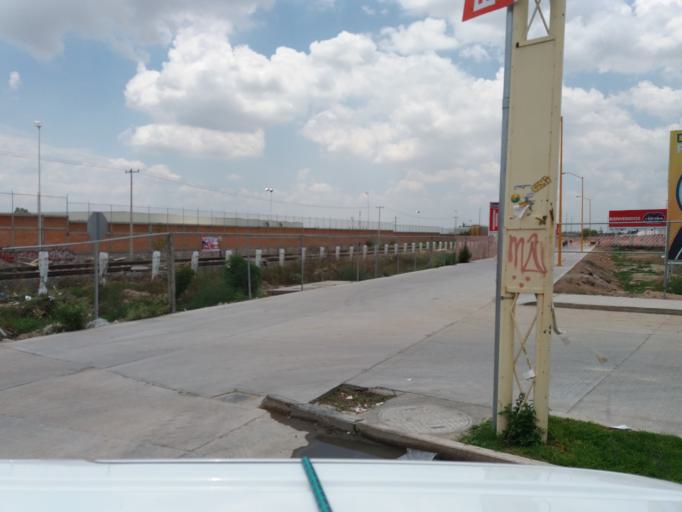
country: MX
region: Aguascalientes
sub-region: Aguascalientes
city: San Sebastian [Fraccionamiento]
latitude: 21.8054
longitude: -102.2764
